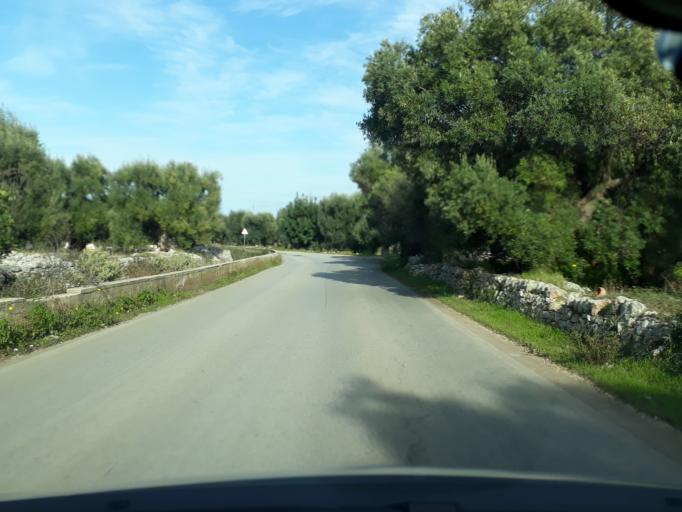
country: IT
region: Apulia
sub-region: Provincia di Brindisi
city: Fasano
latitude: 40.8216
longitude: 17.3589
